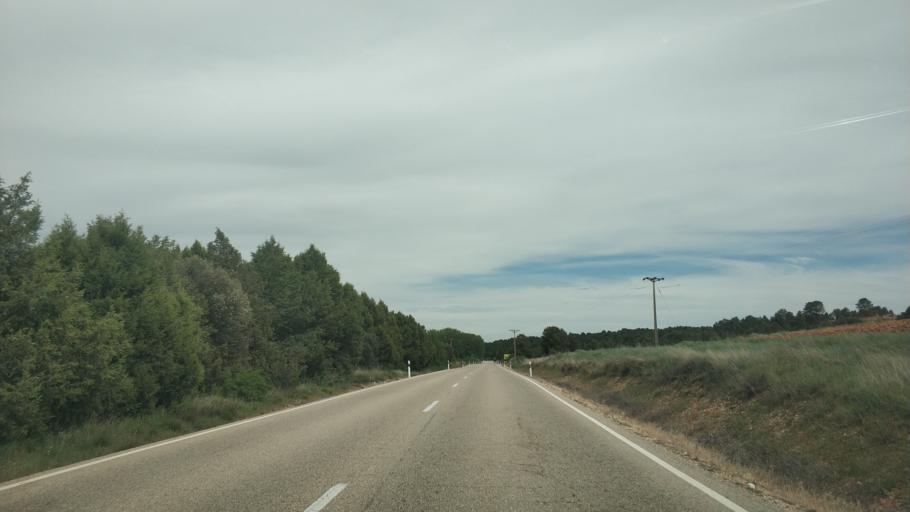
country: ES
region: Castille and Leon
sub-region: Provincia de Soria
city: Valdenebro
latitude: 41.5675
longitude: -3.0026
